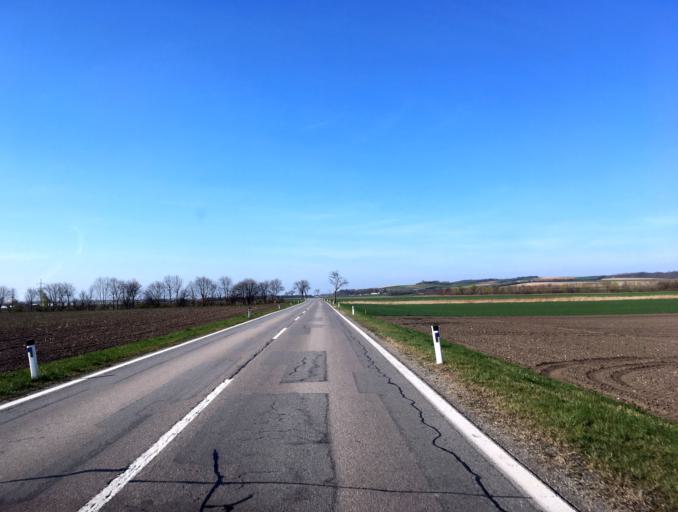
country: AT
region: Lower Austria
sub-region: Politischer Bezirk Bruck an der Leitha
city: Trautmannsdorf an der Leitha
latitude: 48.0432
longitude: 16.6220
